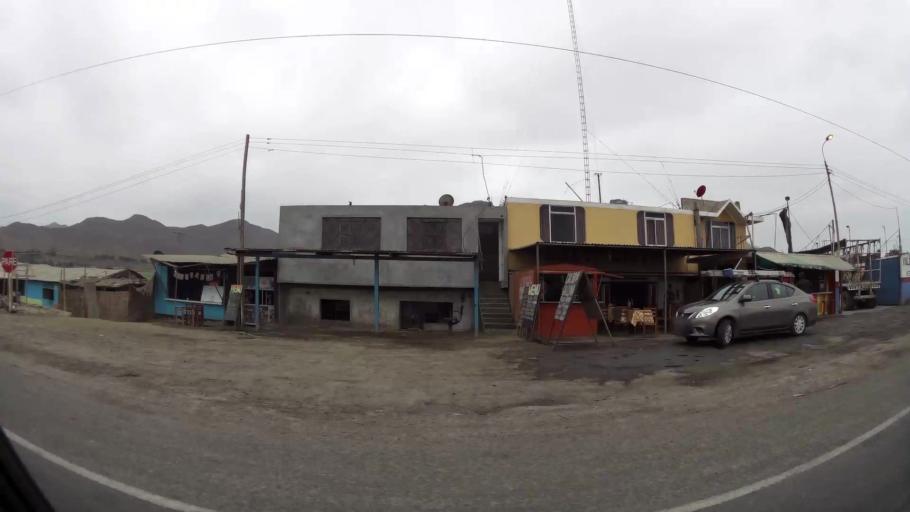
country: PE
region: Lima
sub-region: Barranca
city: Pativilca
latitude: -10.6697
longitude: -77.7941
